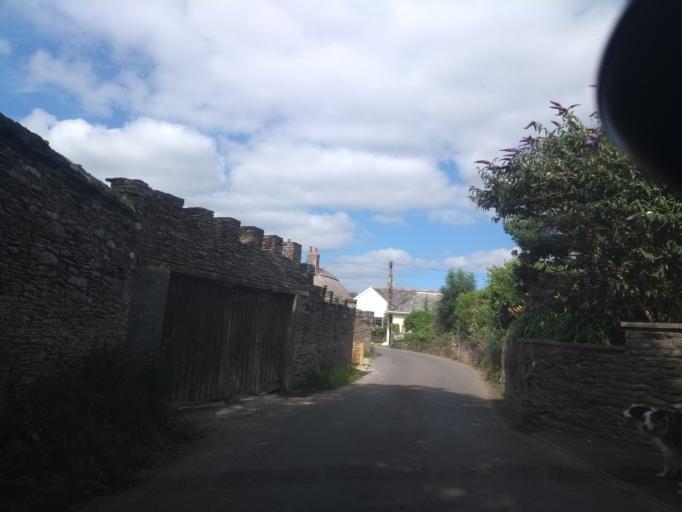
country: GB
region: England
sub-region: Devon
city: Modbury
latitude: 50.2969
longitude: -3.8935
